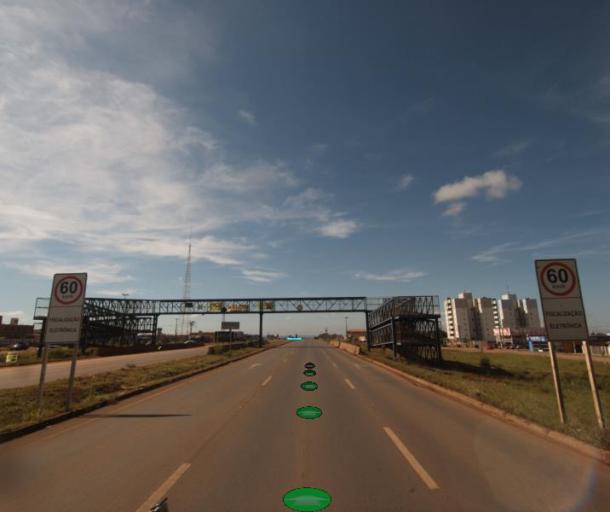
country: BR
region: Federal District
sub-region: Brasilia
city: Brasilia
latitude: -15.7509
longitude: -48.2611
